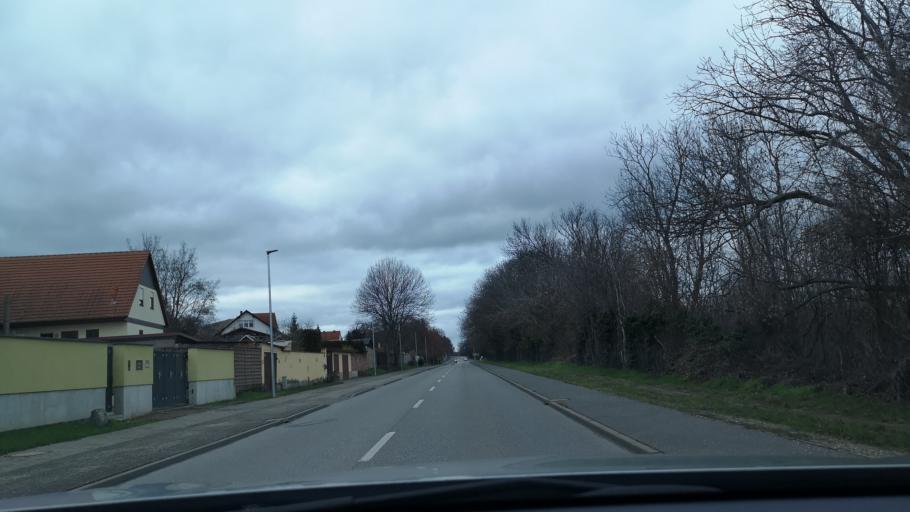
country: DE
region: Saxony-Anhalt
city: Krumpa
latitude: 51.2961
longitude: 11.8485
